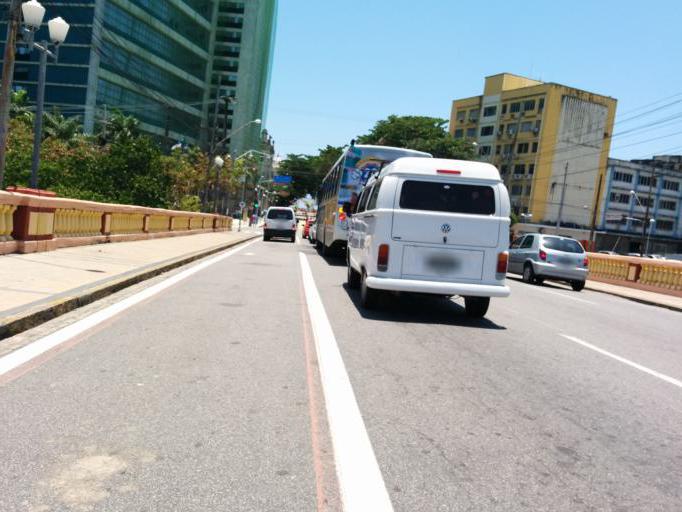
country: BR
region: Pernambuco
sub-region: Recife
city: Recife
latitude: -8.0622
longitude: -34.8744
